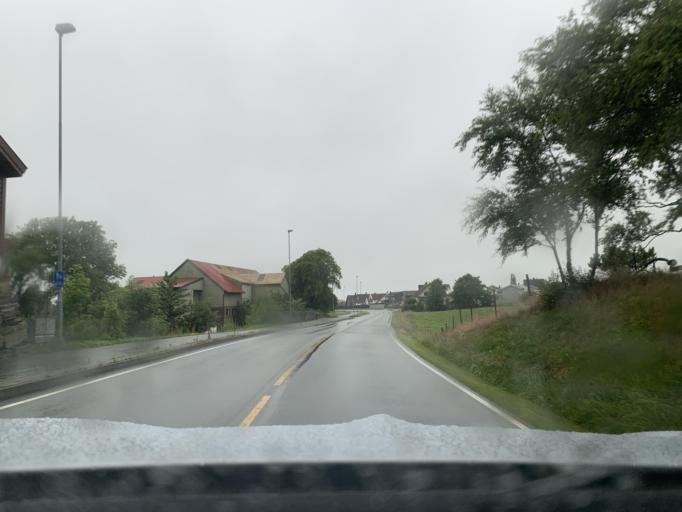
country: NO
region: Rogaland
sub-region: Time
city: Bryne
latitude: 58.7384
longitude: 5.6304
